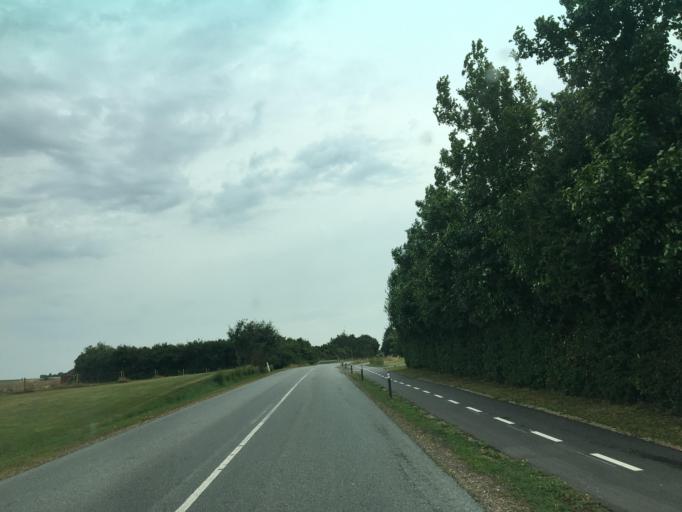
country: DK
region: North Denmark
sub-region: Thisted Kommune
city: Hurup
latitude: 56.8017
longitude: 8.4098
